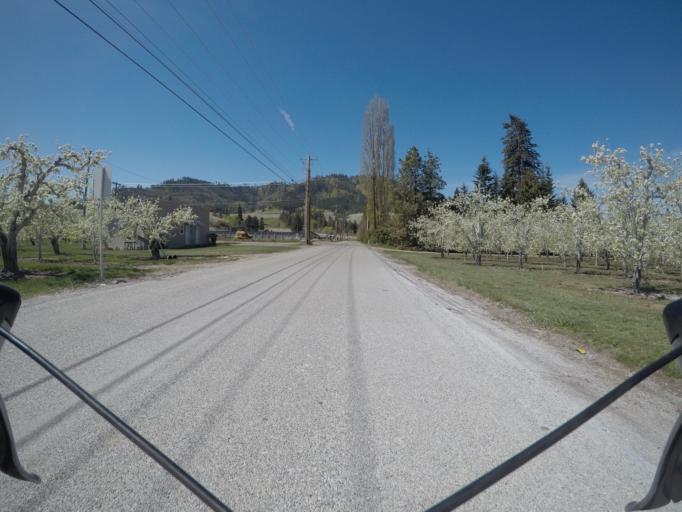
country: US
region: Washington
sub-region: Chelan County
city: Leavenworth
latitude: 47.5642
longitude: -120.5977
